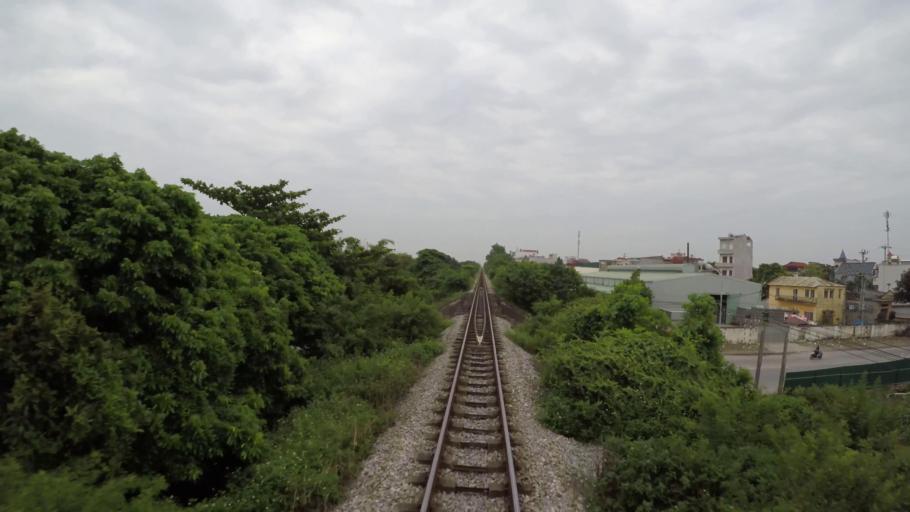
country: VN
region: Hai Duong
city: Thanh Pho Hai Duong
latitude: 20.9494
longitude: 106.3619
